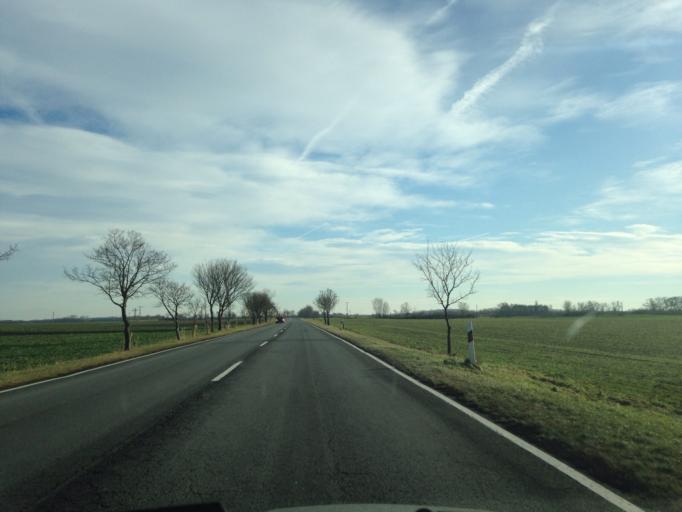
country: HU
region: Gyor-Moson-Sopron
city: Kimle
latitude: 47.8042
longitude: 17.3725
